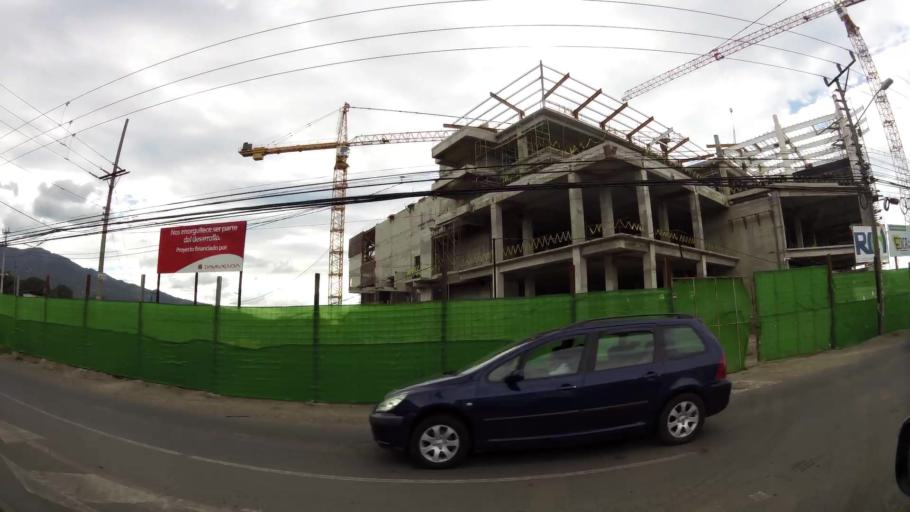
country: CR
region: San Jose
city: Santa Ana
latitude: 9.9573
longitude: -84.1958
